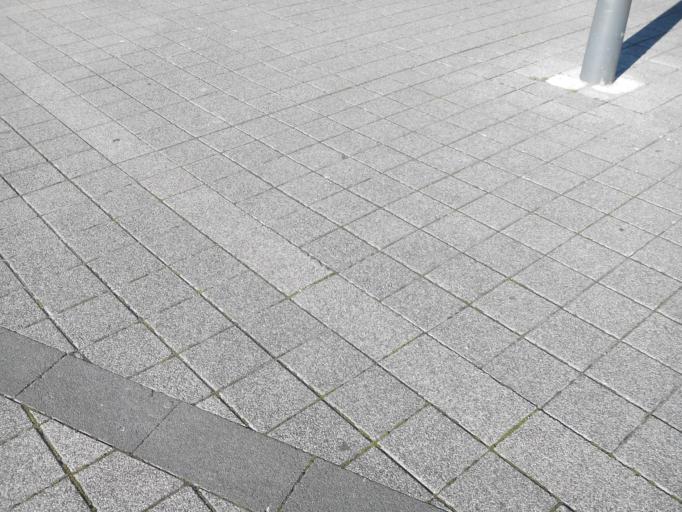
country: FR
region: Centre
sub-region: Departement d'Indre-et-Loire
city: La Riche
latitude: 47.3888
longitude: 0.6583
